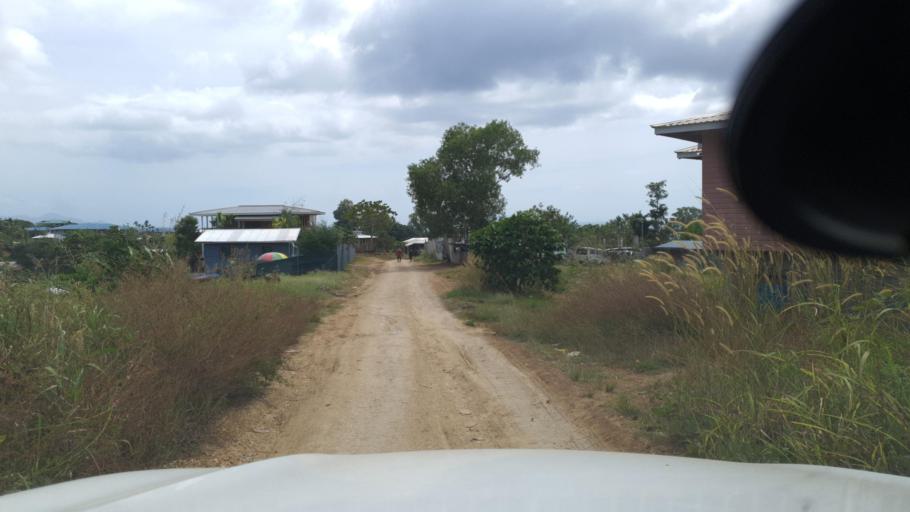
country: SB
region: Guadalcanal
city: Honiara
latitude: -9.4346
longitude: 159.9291
